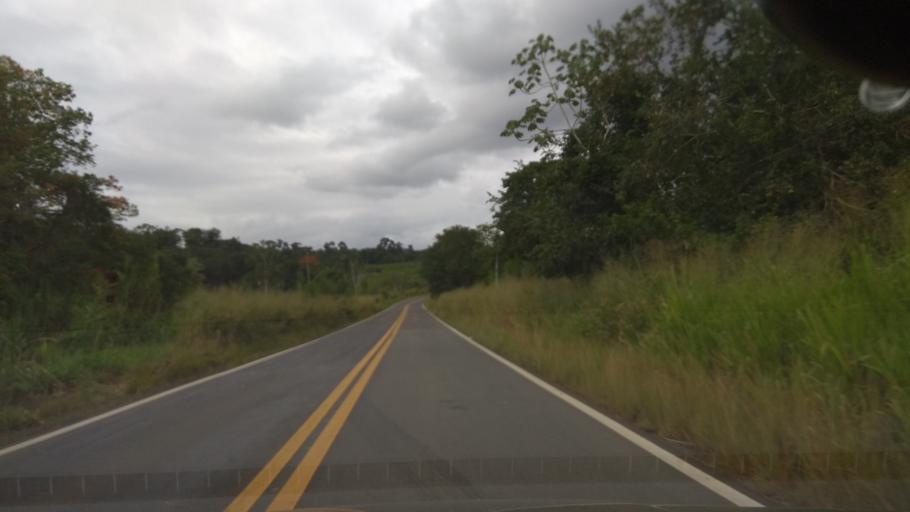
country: BR
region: Bahia
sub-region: Ubata
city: Ubata
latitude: -14.2048
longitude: -39.5748
